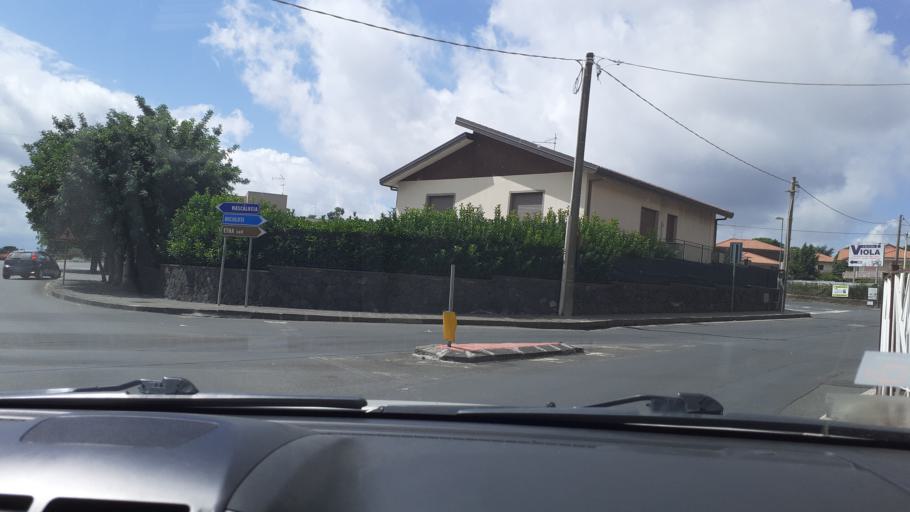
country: IT
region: Sicily
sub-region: Catania
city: Pedara
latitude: 37.6135
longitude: 15.0566
